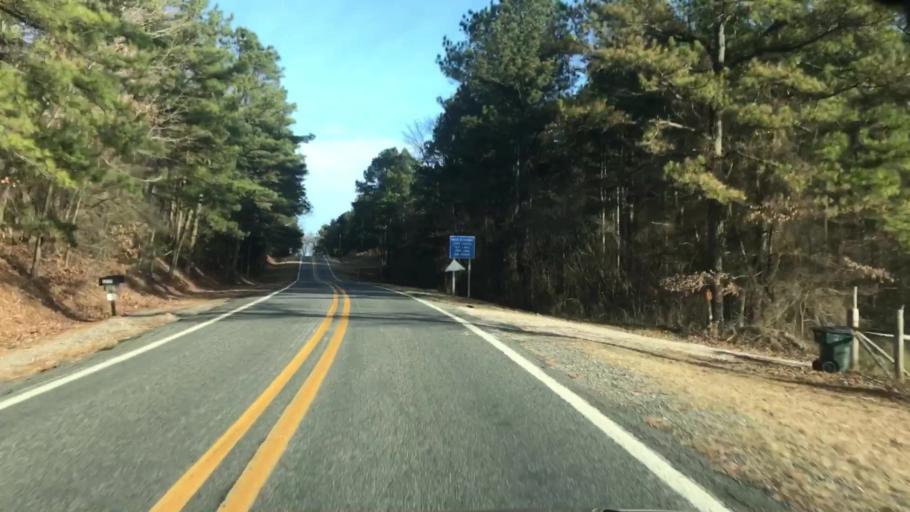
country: US
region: Arkansas
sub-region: Garland County
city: Rockwell
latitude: 34.4826
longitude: -93.2732
